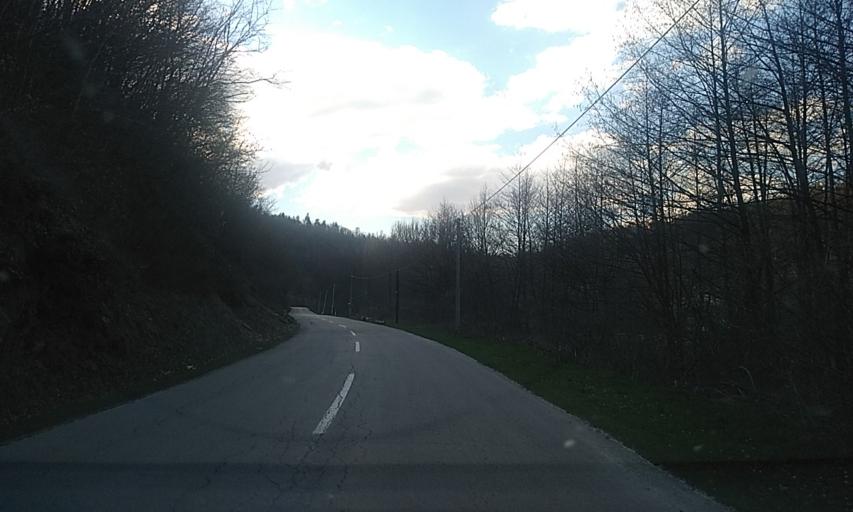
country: RS
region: Central Serbia
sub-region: Pcinjski Okrug
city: Bosilegrad
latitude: 42.4293
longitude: 22.5172
